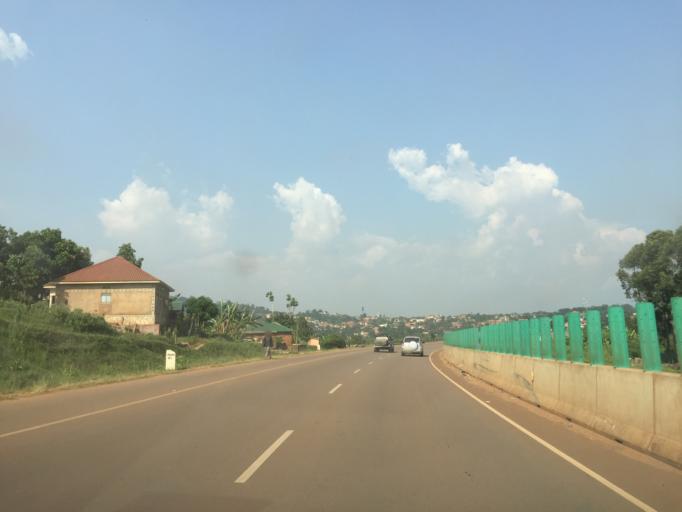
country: UG
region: Central Region
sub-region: Kampala District
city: Kampala
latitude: 0.2351
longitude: 32.6087
